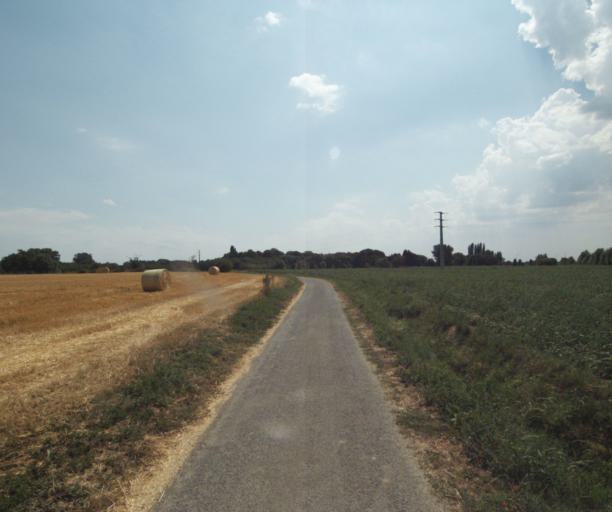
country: FR
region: Nord-Pas-de-Calais
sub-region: Departement du Nord
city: Wervicq-Sud
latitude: 50.7609
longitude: 3.0299
